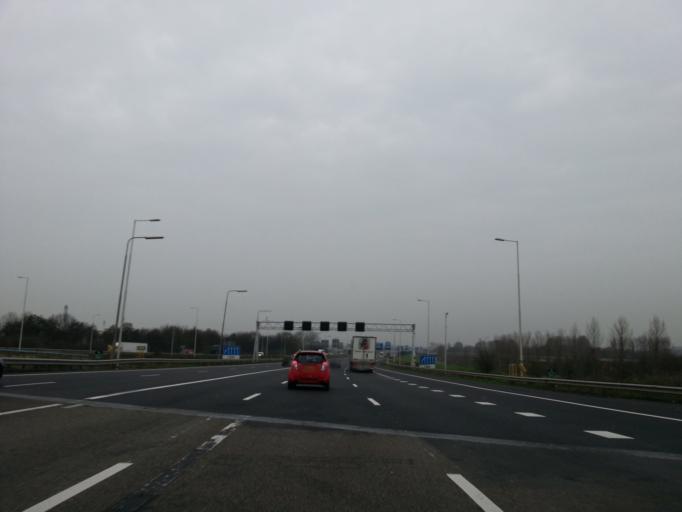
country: NL
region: South Holland
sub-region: Gemeente Schiedam
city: Schiedam
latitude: 51.8781
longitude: 4.3858
